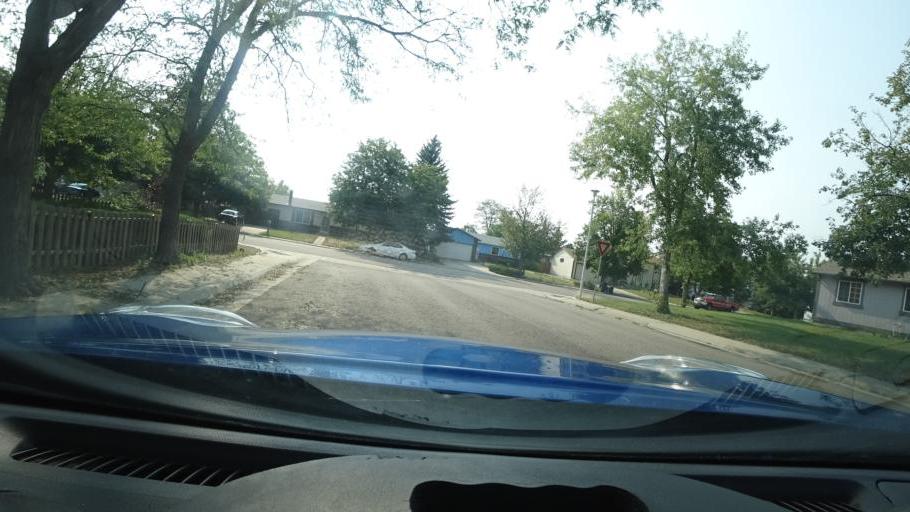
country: US
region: Colorado
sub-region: Adams County
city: Aurora
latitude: 39.6663
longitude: -104.8014
